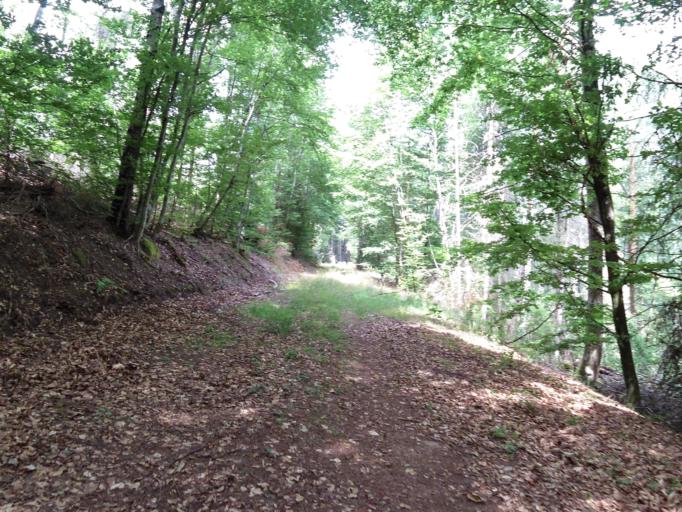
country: DE
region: Rheinland-Pfalz
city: Elmstein
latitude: 49.3776
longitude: 7.9313
